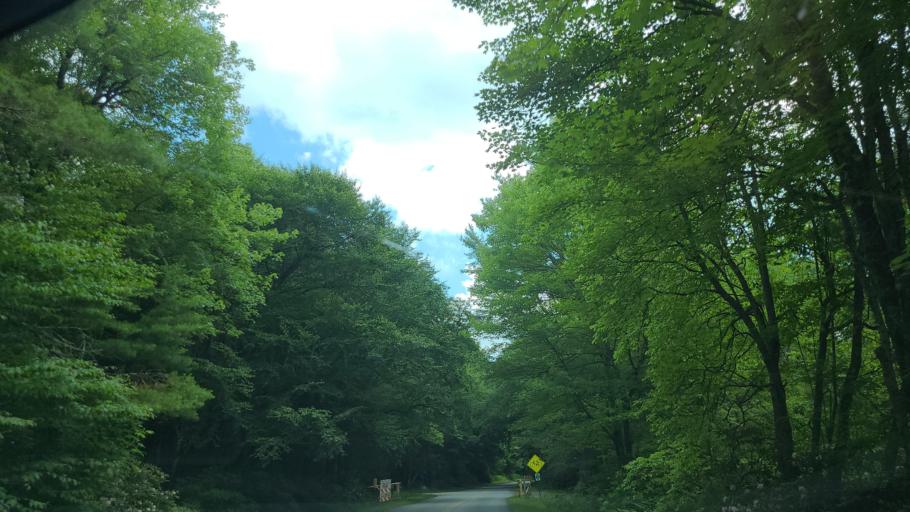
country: US
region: North Carolina
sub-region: Avery County
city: Newland
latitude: 35.9845
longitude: -81.9109
